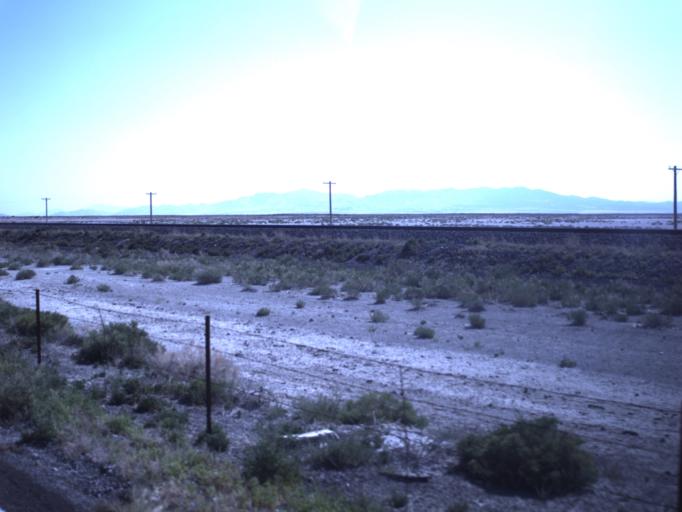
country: US
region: Utah
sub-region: Millard County
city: Delta
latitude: 39.1834
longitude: -112.6984
